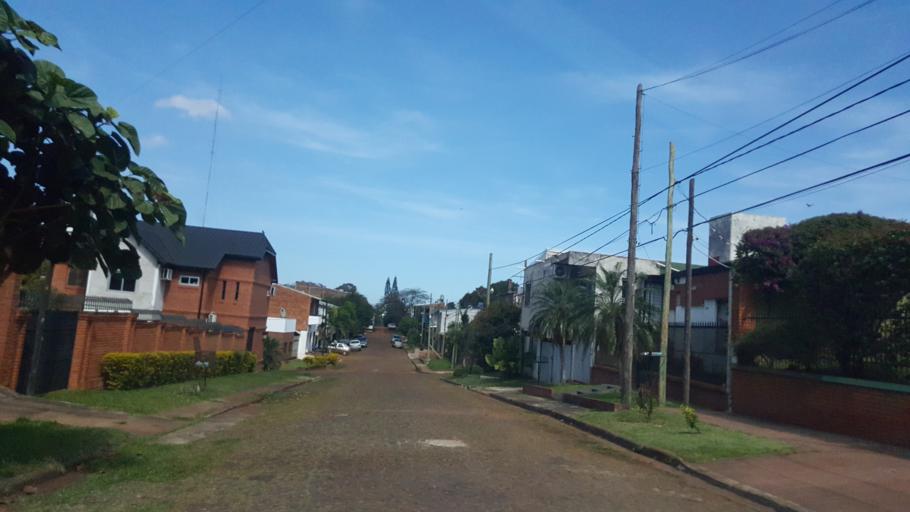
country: AR
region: Misiones
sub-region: Departamento de Capital
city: Posadas
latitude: -27.3942
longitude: -55.9108
